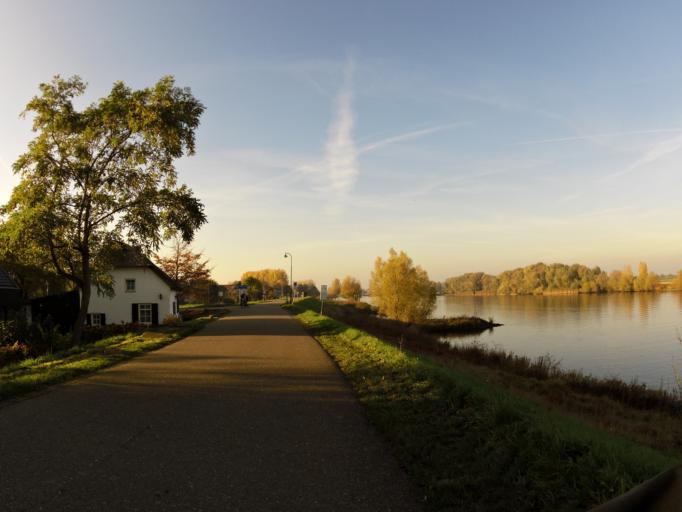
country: NL
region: Gelderland
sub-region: Gemeente Maasdriel
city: Hedel
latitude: 51.7340
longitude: 5.2424
